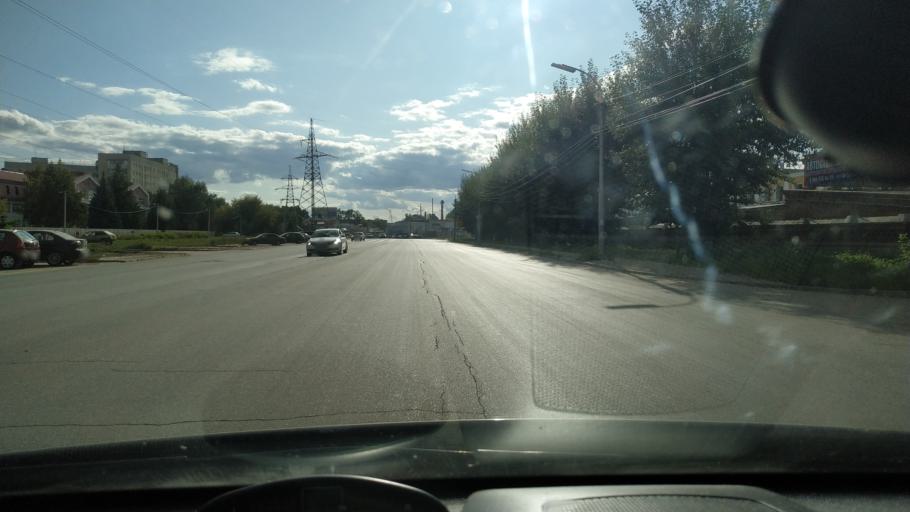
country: RU
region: Rjazan
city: Ryazan'
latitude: 54.6186
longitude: 39.6966
